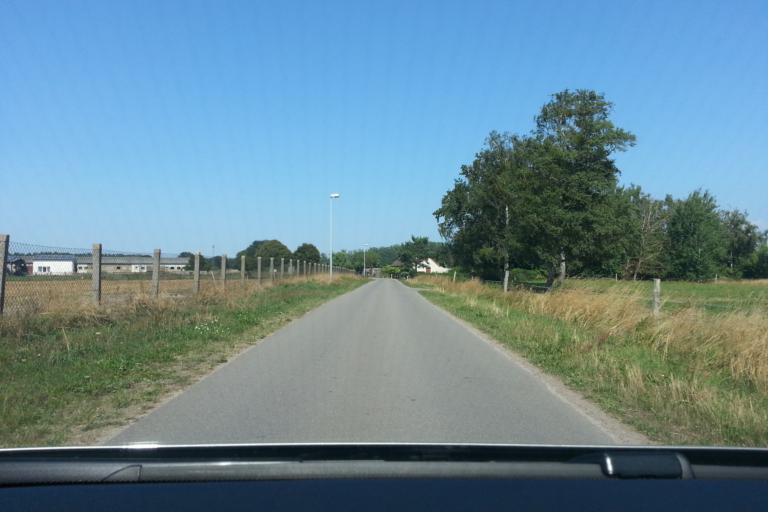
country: DE
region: Mecklenburg-Vorpommern
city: Ducherow
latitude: 53.7143
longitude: 13.7924
